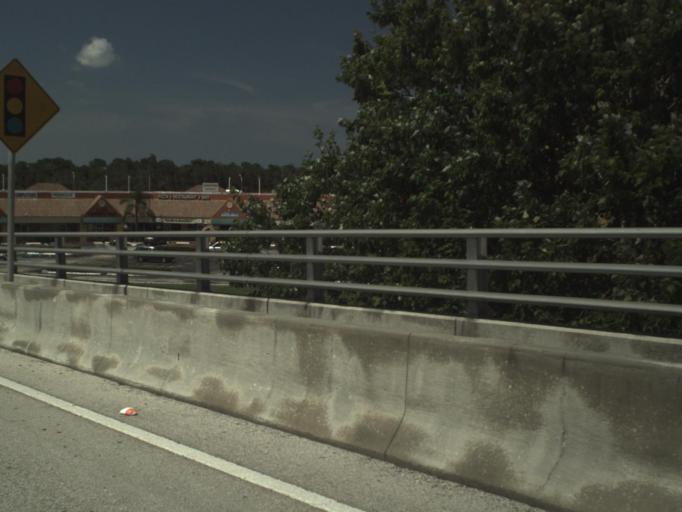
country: US
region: Florida
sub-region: Martin County
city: North River Shores
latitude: 27.2135
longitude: -80.2601
